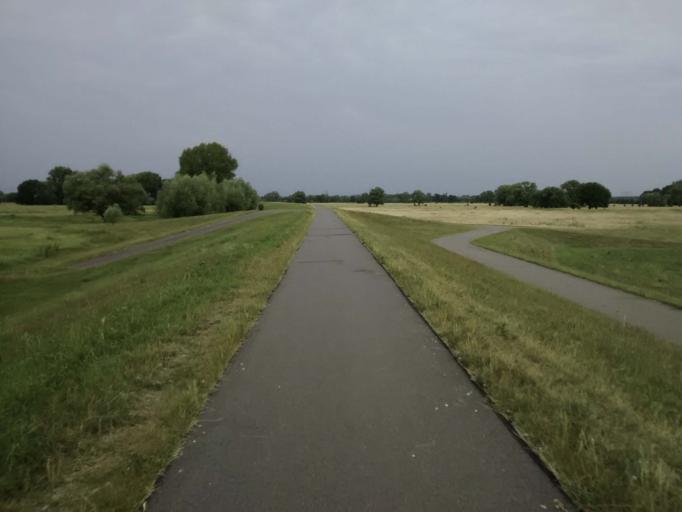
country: DE
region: Brandenburg
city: Breese
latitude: 52.9667
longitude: 11.7897
